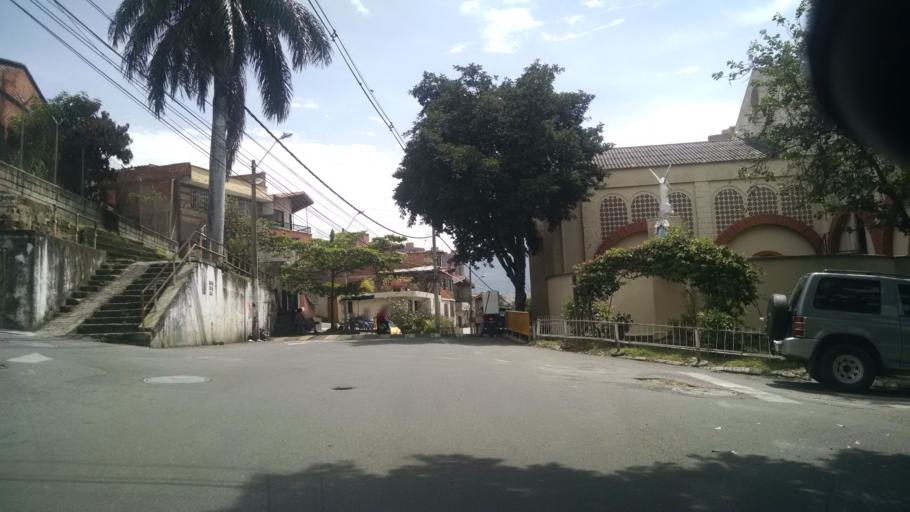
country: CO
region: Antioquia
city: Medellin
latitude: 6.2624
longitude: -75.6063
